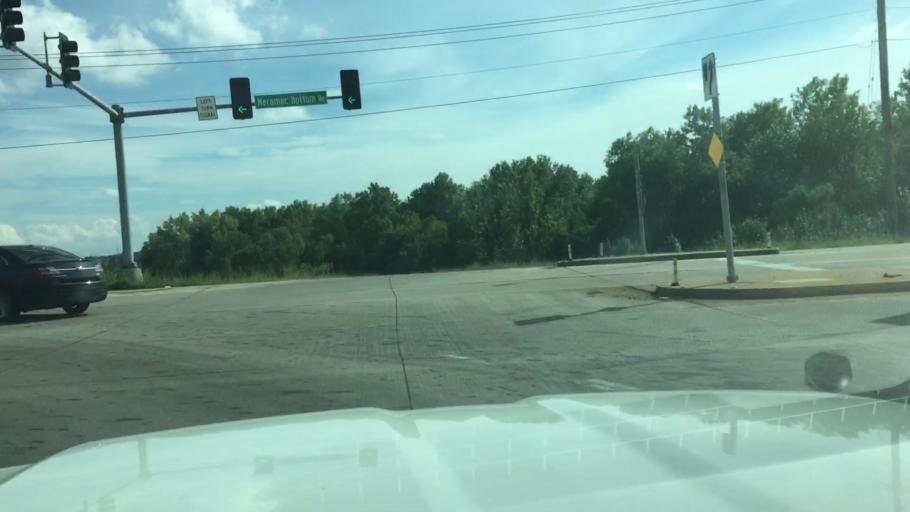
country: US
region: Missouri
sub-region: Jefferson County
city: Arnold
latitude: 38.4620
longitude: -90.3751
